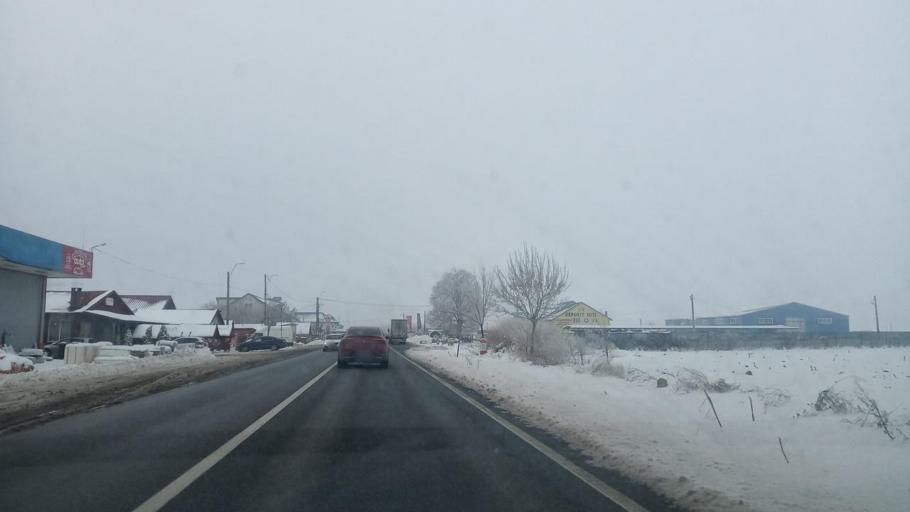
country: RO
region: Iasi
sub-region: Comuna Ciohorani
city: Ciohorani
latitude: 47.0969
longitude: 26.7011
